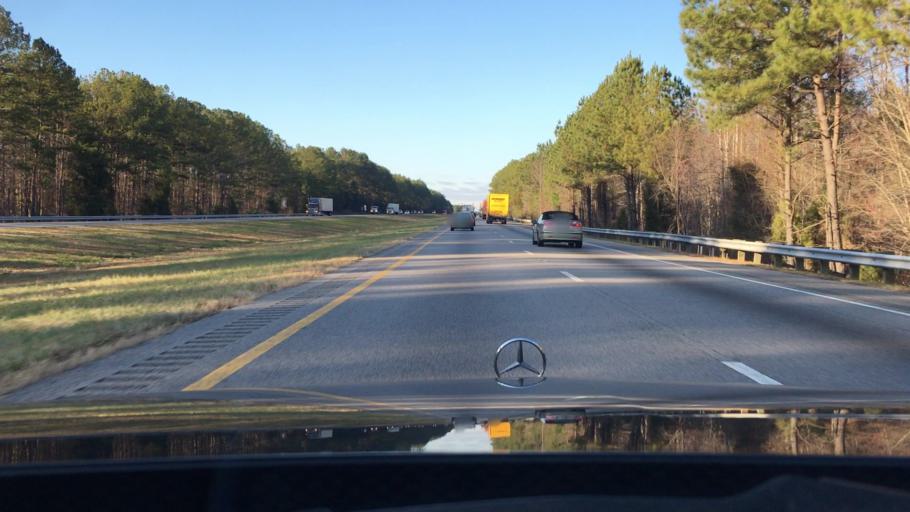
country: US
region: South Carolina
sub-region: Chester County
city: Eureka Mill
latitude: 34.7327
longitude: -81.0340
